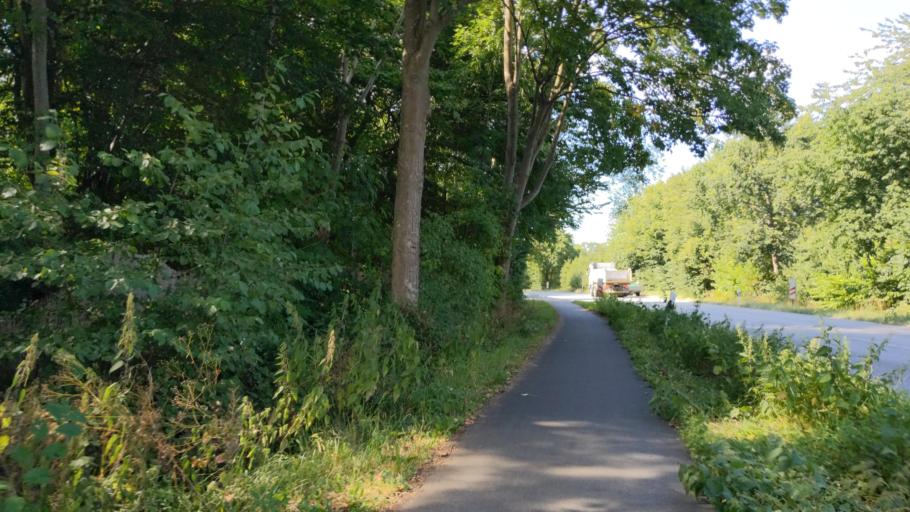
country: DE
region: Schleswig-Holstein
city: Dornick
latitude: 54.1547
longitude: 10.3844
